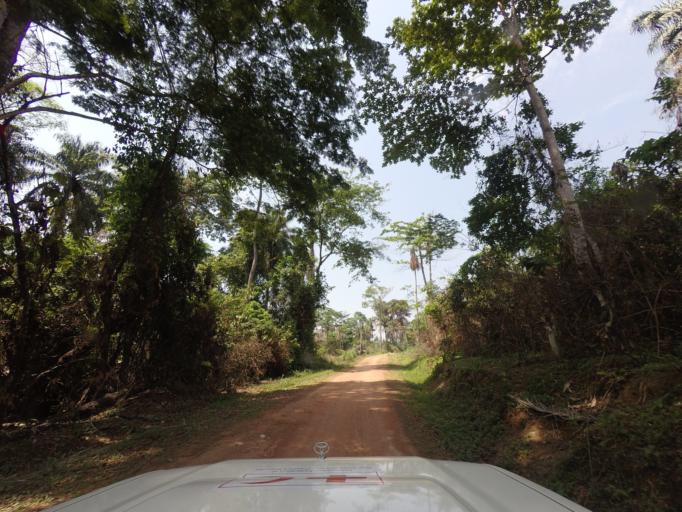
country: LR
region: Lofa
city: Voinjama
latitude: 8.4429
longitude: -9.6880
